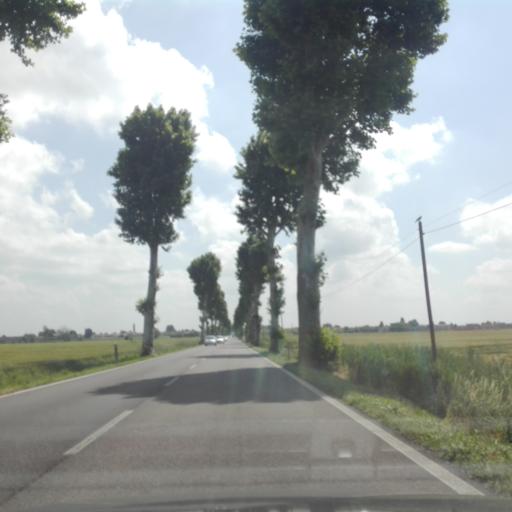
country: IT
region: Veneto
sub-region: Provincia di Rovigo
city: Buso
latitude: 45.0750
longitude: 11.8686
